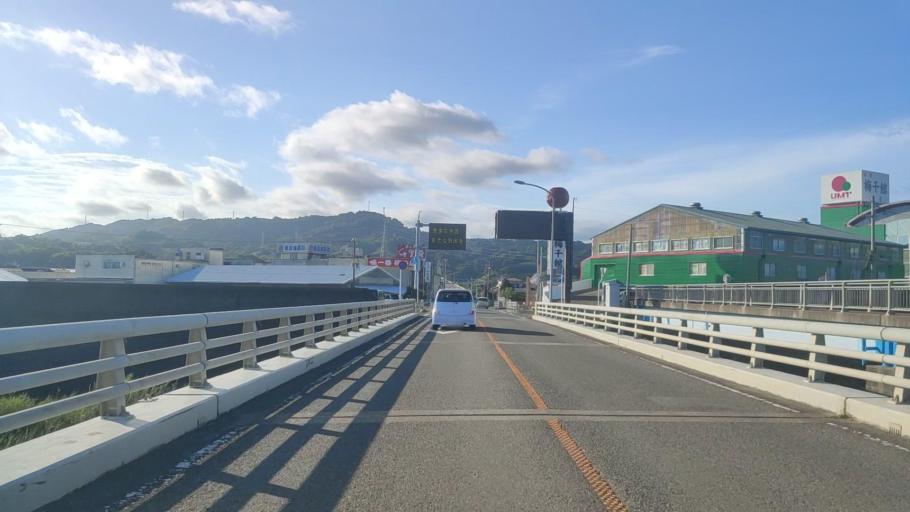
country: JP
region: Wakayama
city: Tanabe
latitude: 33.7721
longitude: 135.3136
